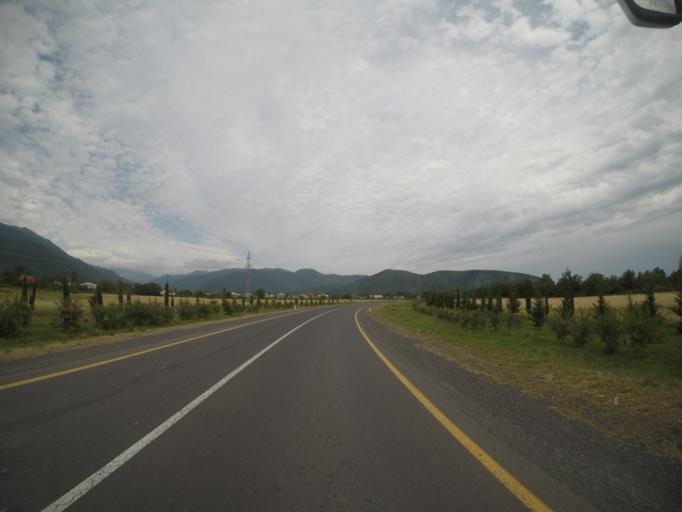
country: AZ
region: Qakh Rayon
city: Qax
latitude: 41.4118
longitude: 46.8992
